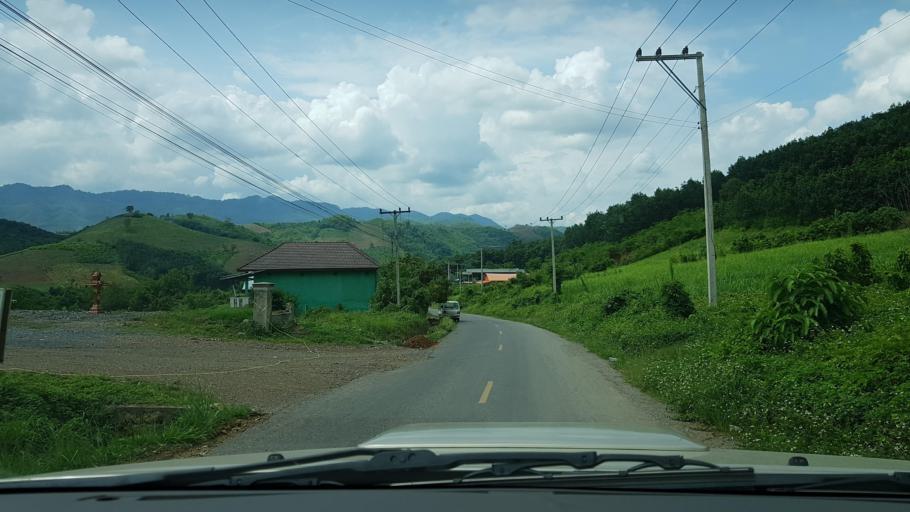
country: LA
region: Loungnamtha
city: Muang Nale
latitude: 20.1576
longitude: 101.5046
